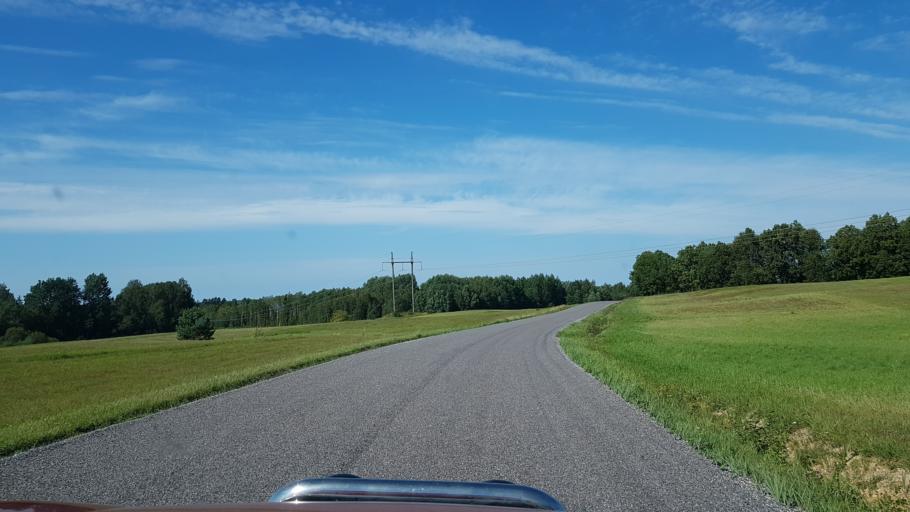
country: EE
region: Tartu
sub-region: Elva linn
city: Elva
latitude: 58.2447
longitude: 26.3891
